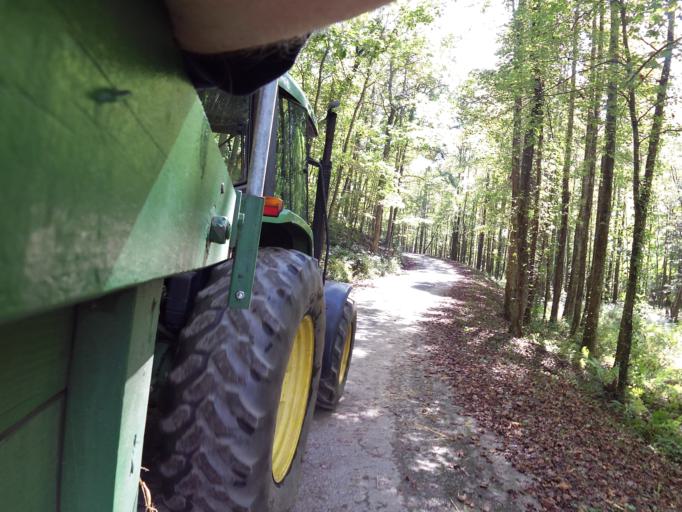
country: US
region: Georgia
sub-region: Dawson County
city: Dawsonville
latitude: 34.5466
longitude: -84.2512
